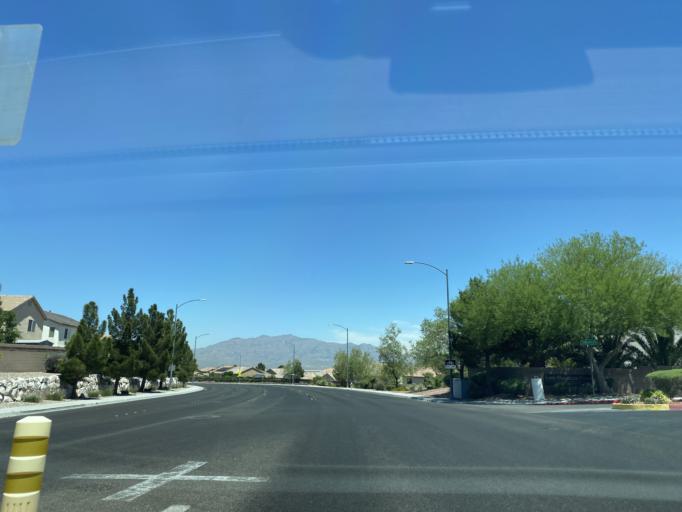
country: US
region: Nevada
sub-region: Clark County
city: Summerlin South
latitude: 36.2398
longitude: -115.3290
